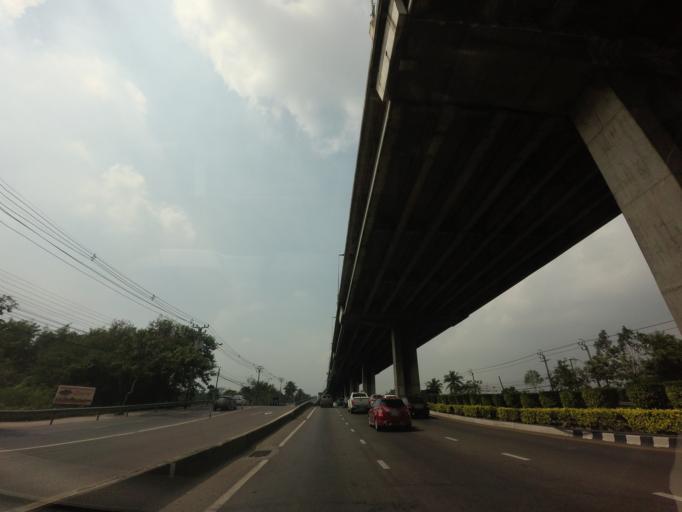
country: TH
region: Bangkok
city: Thawi Watthana
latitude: 13.7862
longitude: 100.3837
